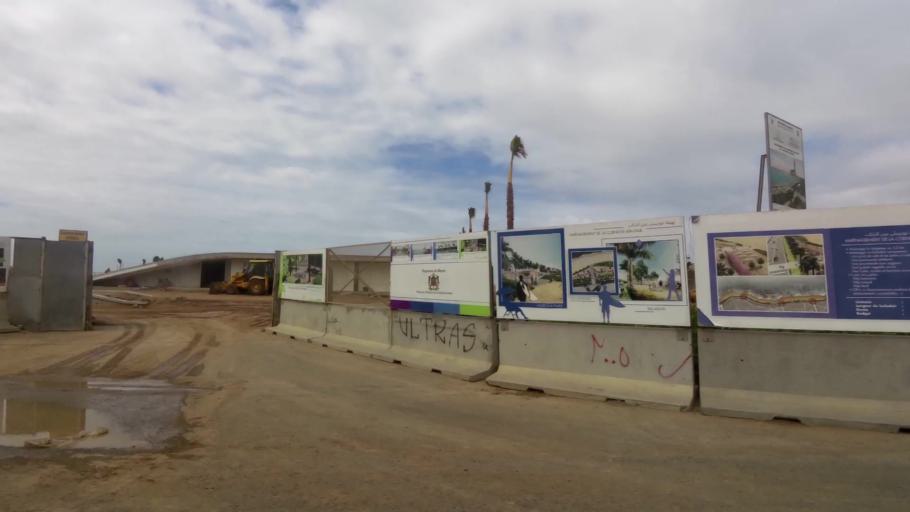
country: MA
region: Grand Casablanca
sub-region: Casablanca
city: Casablanca
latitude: 33.6039
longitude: -7.6399
